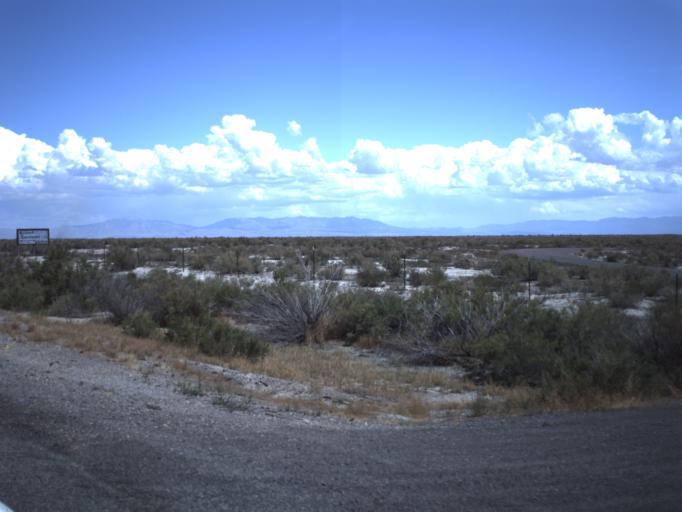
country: US
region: Utah
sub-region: Millard County
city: Delta
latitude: 39.2861
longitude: -112.8359
